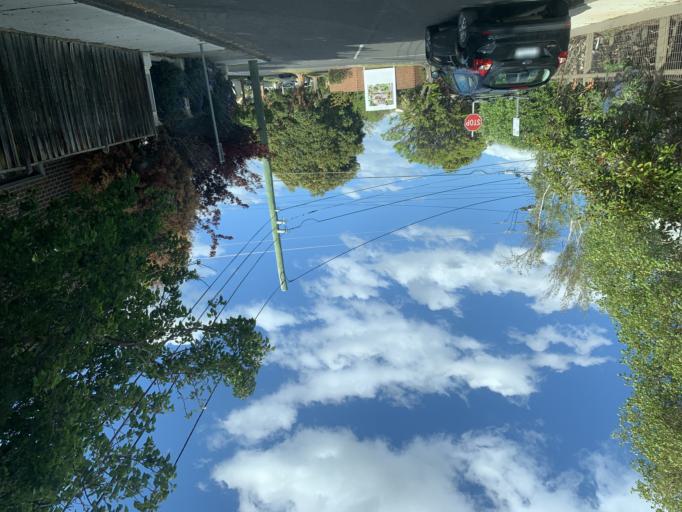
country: AU
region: Victoria
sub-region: Bayside
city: North Brighton
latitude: -37.9136
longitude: 144.9994
